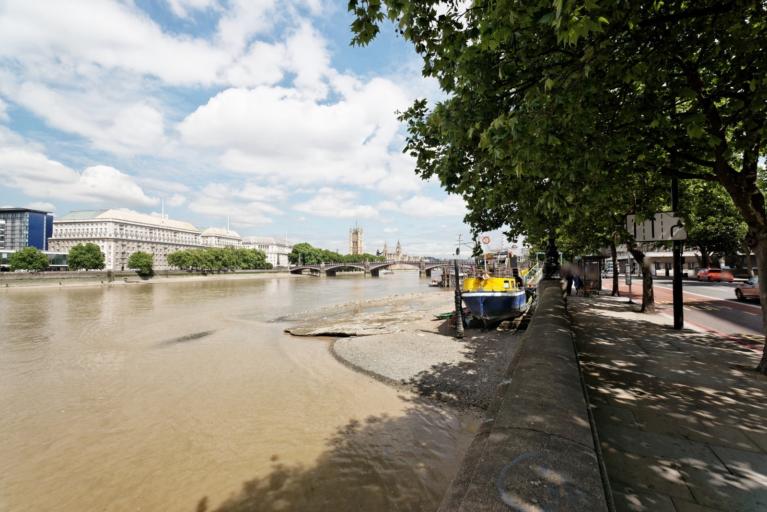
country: GB
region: England
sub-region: Greater London
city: City of Westminster
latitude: 51.4916
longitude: -0.1223
